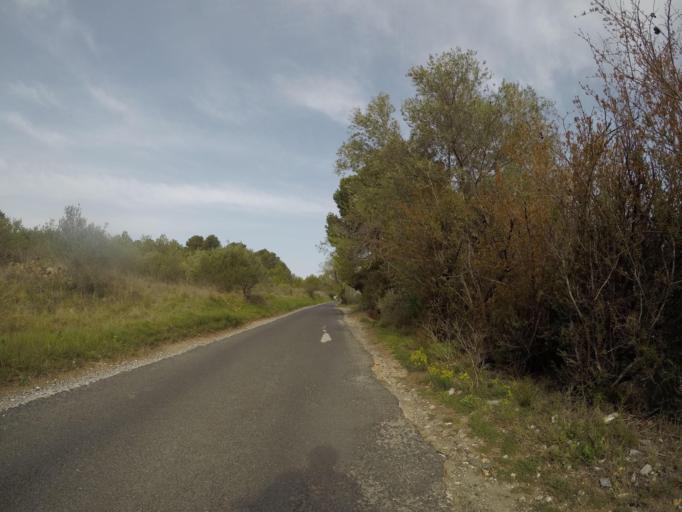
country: FR
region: Languedoc-Roussillon
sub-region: Departement des Pyrenees-Orientales
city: Baixas
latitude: 42.7693
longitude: 2.8076
